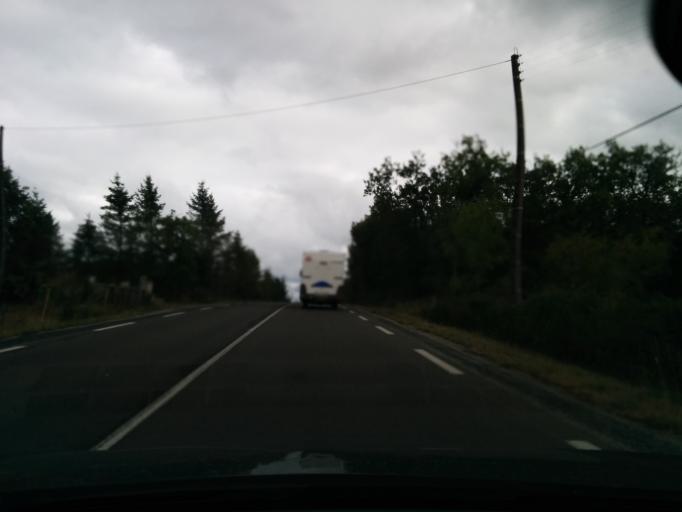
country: FR
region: Midi-Pyrenees
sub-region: Departement du Lot
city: Souillac
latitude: 45.0055
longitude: 1.5180
